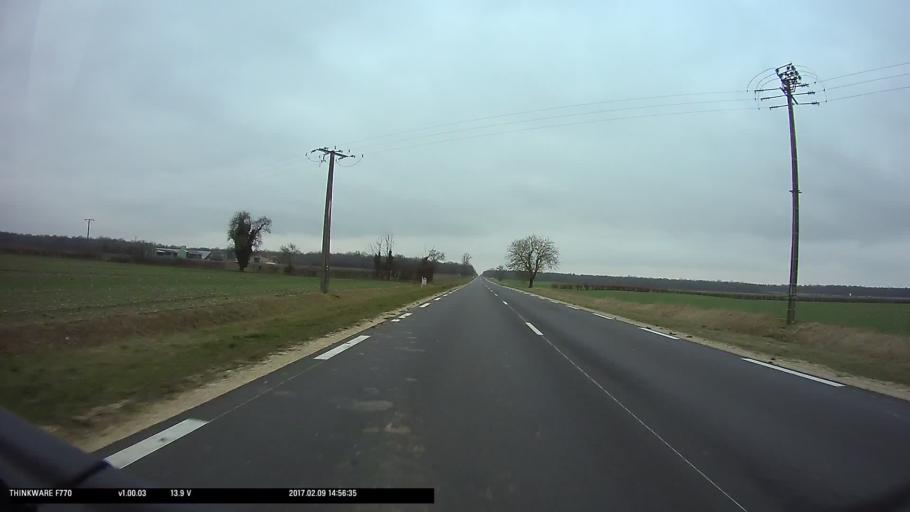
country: FR
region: Centre
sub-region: Departement du Cher
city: Levet
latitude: 46.8642
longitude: 2.4189
